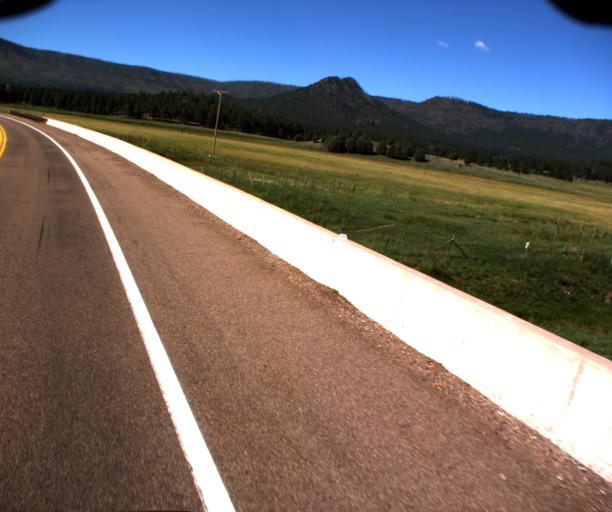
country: US
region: Arizona
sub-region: Apache County
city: Eagar
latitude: 33.9551
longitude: -109.2110
